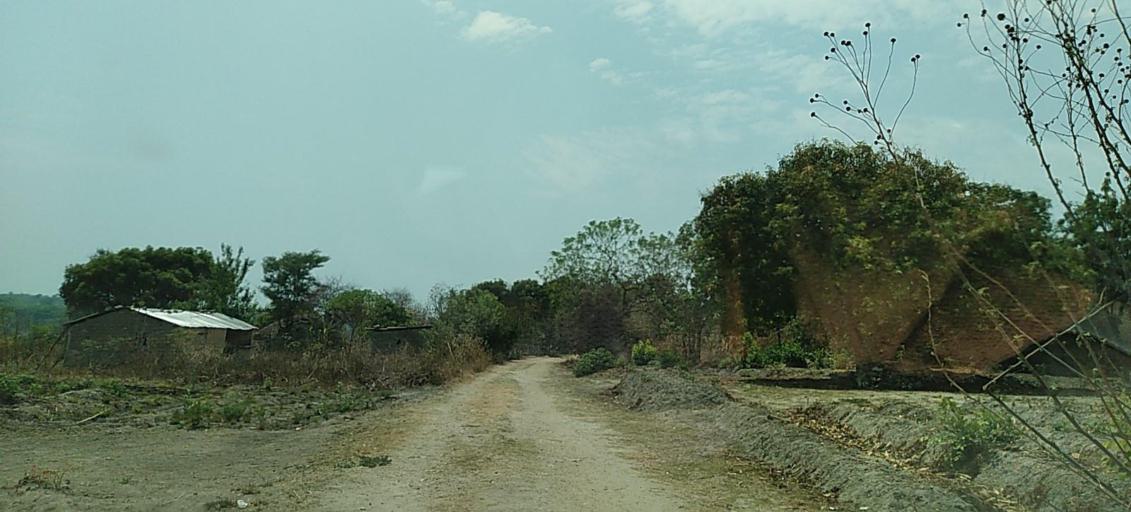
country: ZM
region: Copperbelt
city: Kalulushi
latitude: -12.9547
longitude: 28.1431
